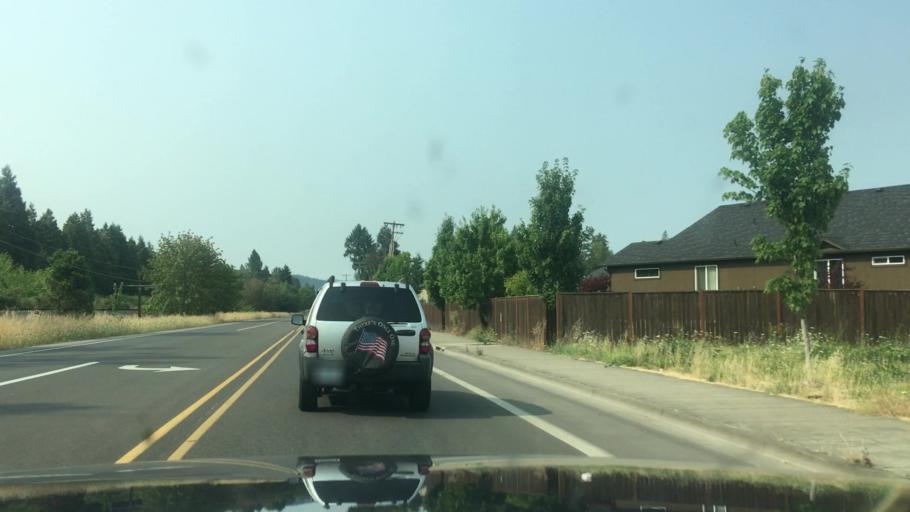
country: US
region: Oregon
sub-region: Lane County
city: Cottage Grove
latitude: 43.7878
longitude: -123.0659
